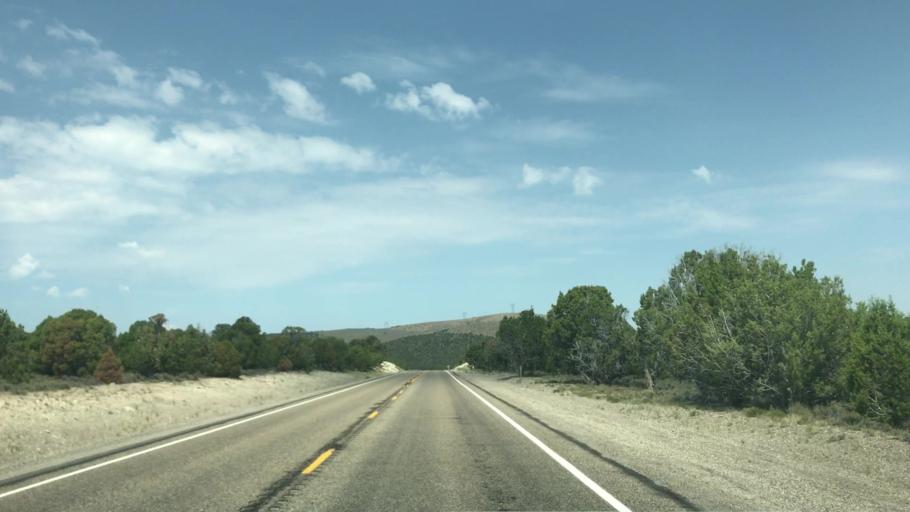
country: US
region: Nevada
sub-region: White Pine County
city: Ely
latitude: 39.3880
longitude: -115.0759
